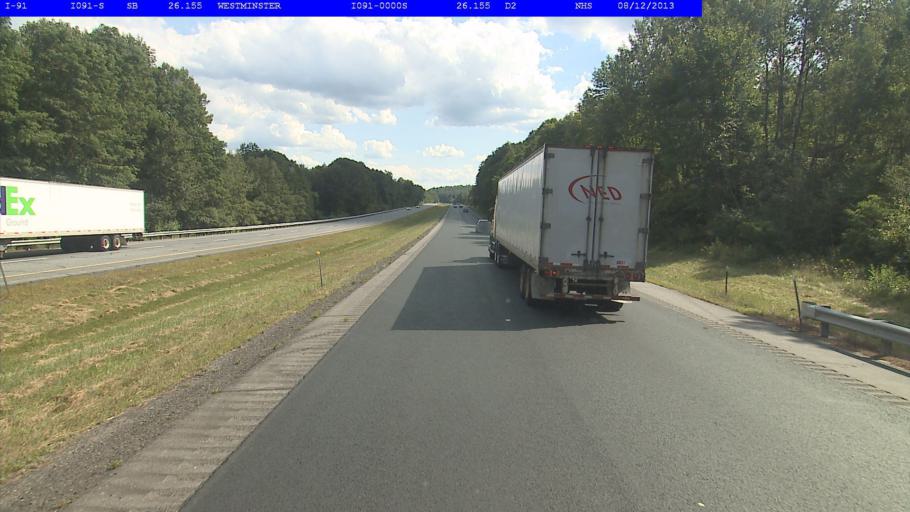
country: US
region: Vermont
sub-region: Windham County
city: Bellows Falls
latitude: 43.0578
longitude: -72.4704
